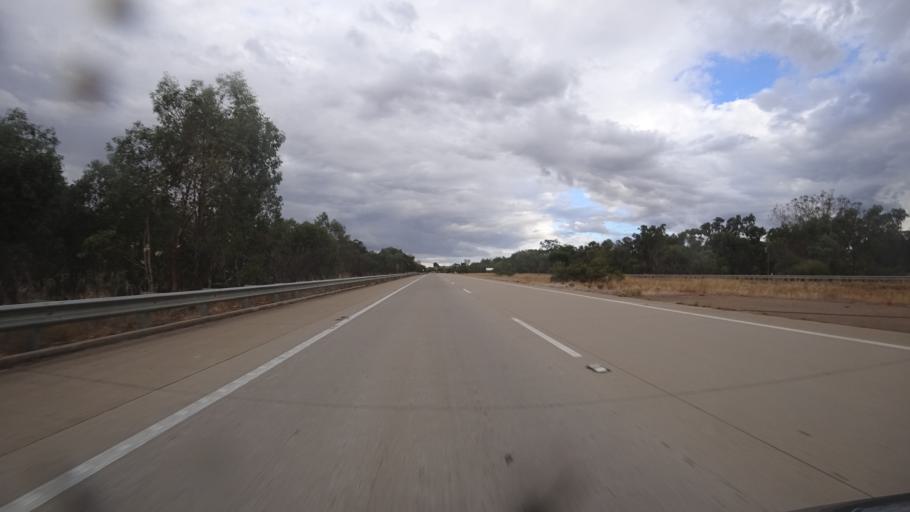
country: AU
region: New South Wales
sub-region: Yass Valley
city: Yass
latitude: -34.8131
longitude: 148.6421
